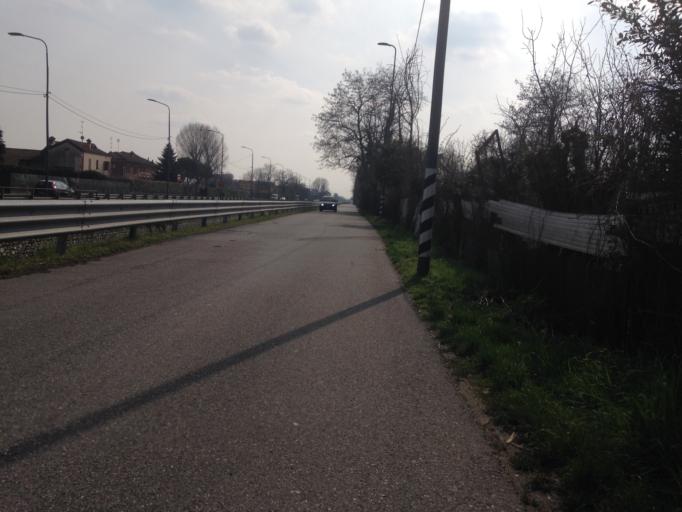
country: IT
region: Lombardy
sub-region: Citta metropolitana di Milano
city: Rozzano
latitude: 45.4217
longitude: 9.1668
